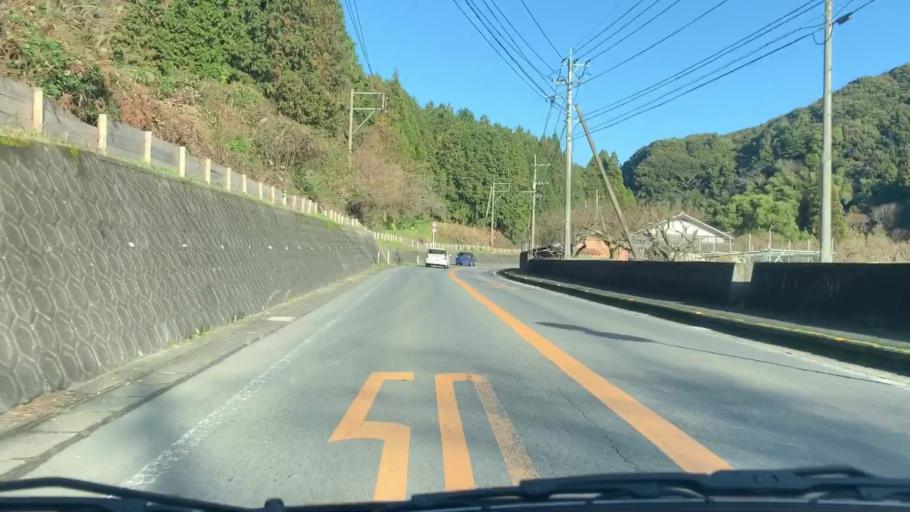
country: JP
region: Saga Prefecture
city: Takeocho-takeo
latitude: 33.2356
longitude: 130.0125
